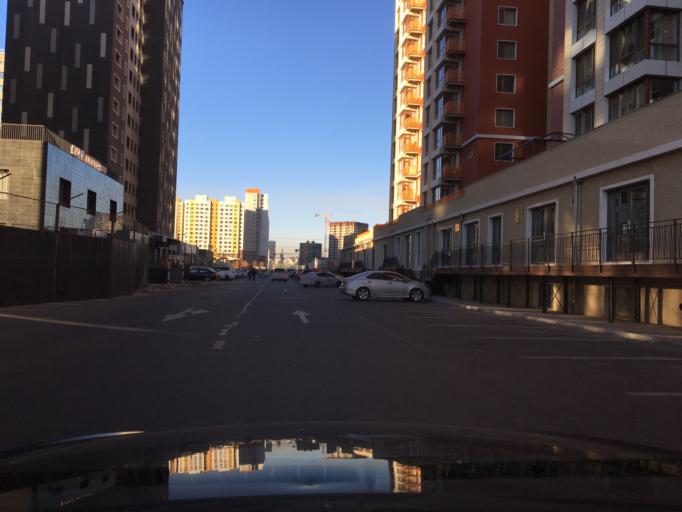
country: MN
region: Ulaanbaatar
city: Ulaanbaatar
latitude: 47.8907
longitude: 106.9237
